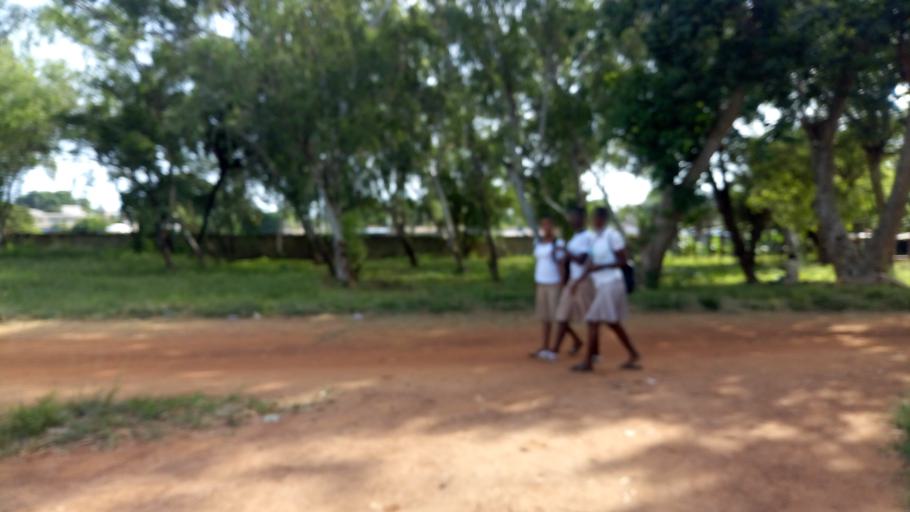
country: TG
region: Maritime
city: Lome
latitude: 6.1906
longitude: 1.1618
